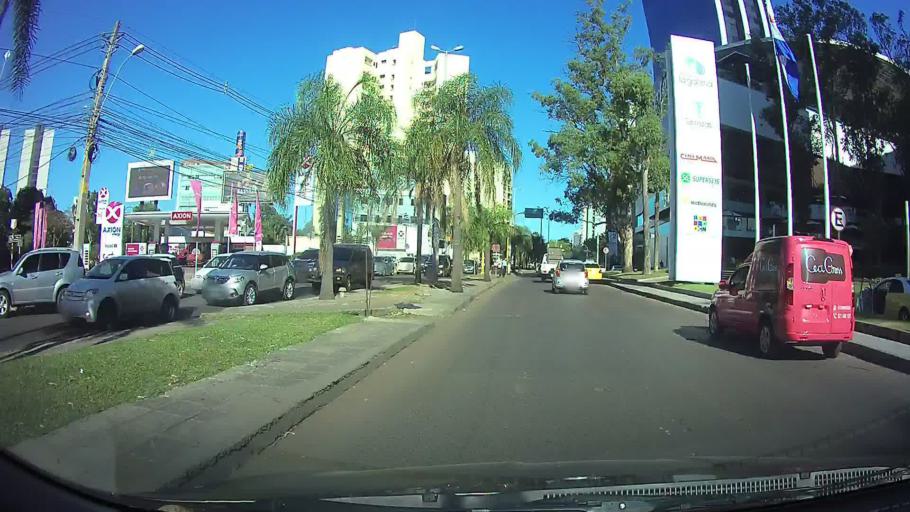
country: PY
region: Central
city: Fernando de la Mora
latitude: -25.2837
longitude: -57.5640
